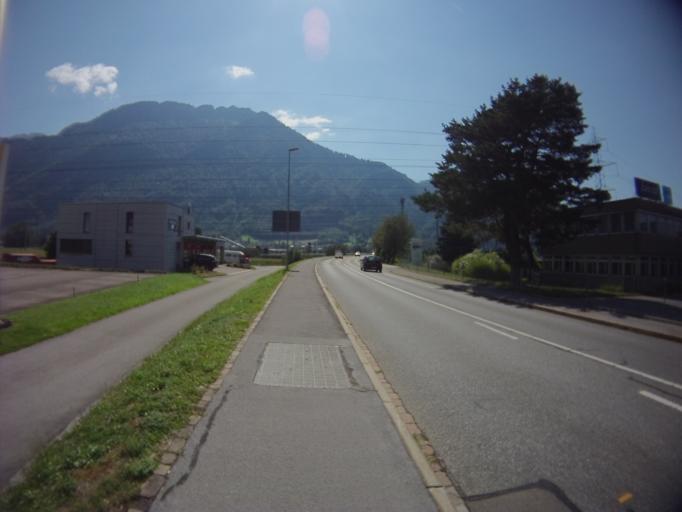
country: CH
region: Glarus
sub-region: Glarus
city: Bilten
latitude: 47.1550
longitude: 9.0367
